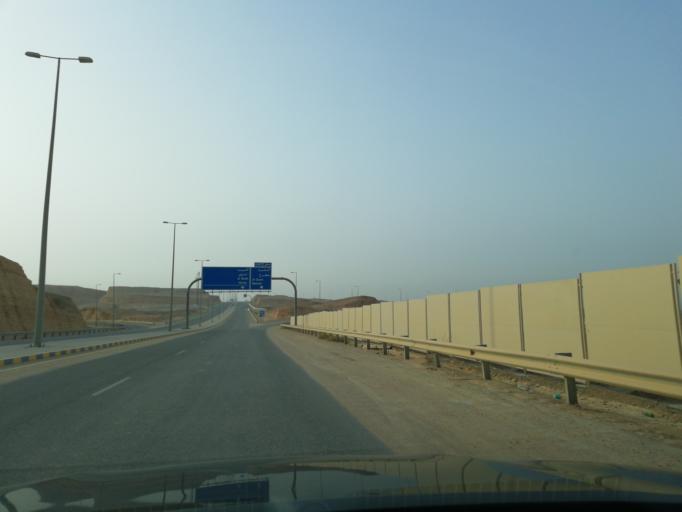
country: OM
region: Muhafazat Masqat
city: Bawshar
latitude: 23.5474
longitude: 58.2939
